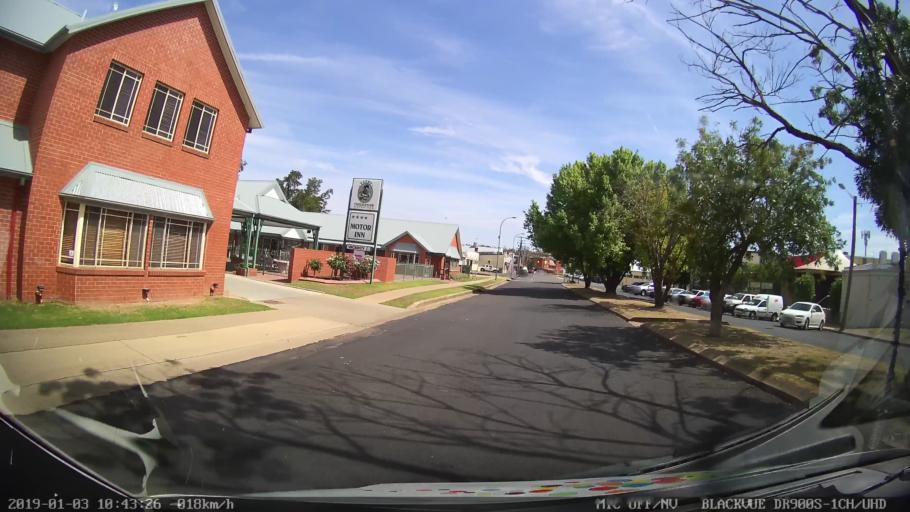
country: AU
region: New South Wales
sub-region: Young
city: Young
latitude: -34.3151
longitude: 148.2958
